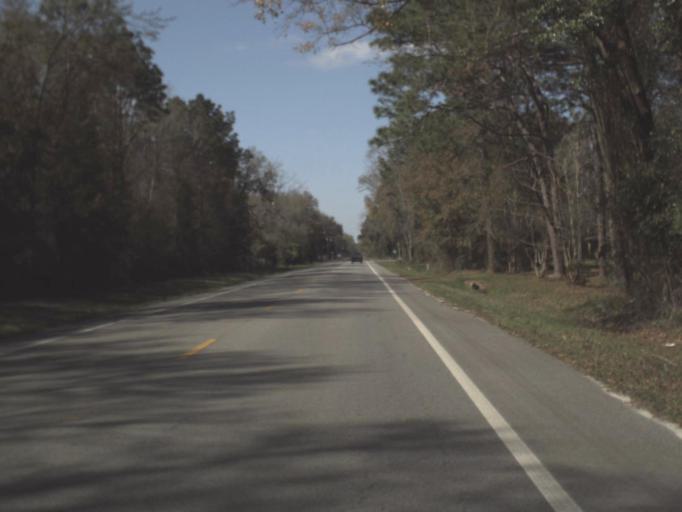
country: US
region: Florida
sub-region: Gulf County
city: Wewahitchka
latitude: 30.0541
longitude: -85.1885
